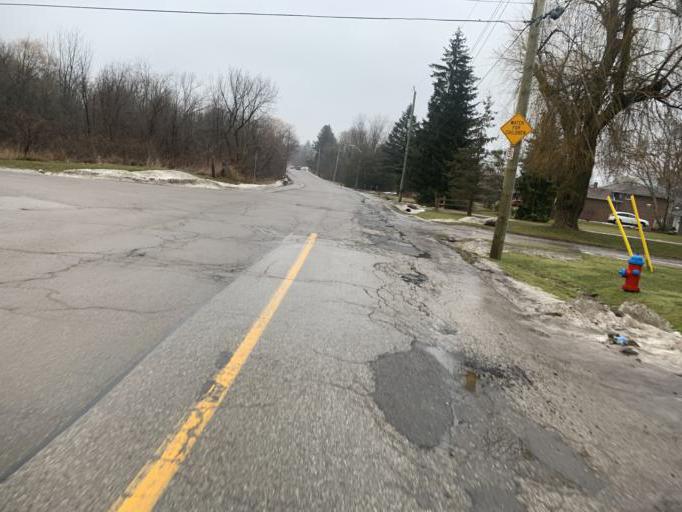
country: CA
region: Ontario
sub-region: Halton
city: Milton
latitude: 43.6578
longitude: -79.9343
